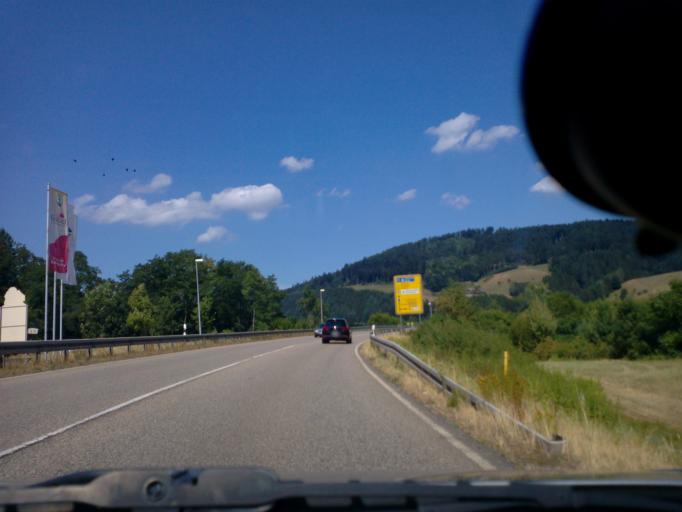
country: DE
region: Baden-Wuerttemberg
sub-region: Freiburg Region
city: Hausach
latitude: 48.2837
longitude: 8.1929
